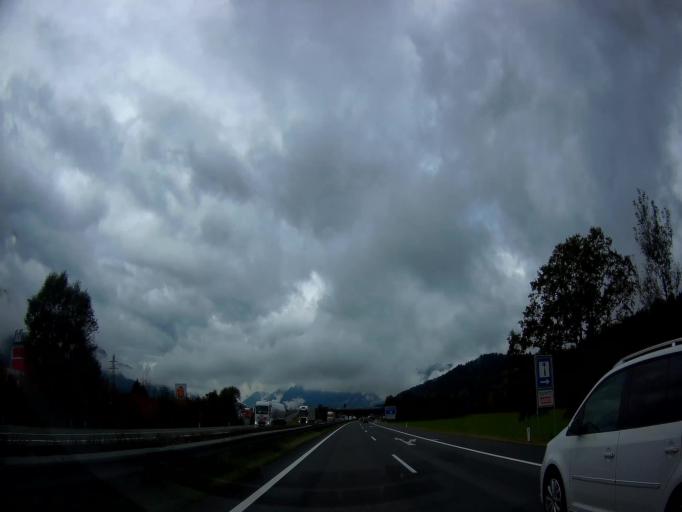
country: AT
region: Tyrol
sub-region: Politischer Bezirk Kufstein
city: Worgl
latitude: 47.4840
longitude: 12.0312
